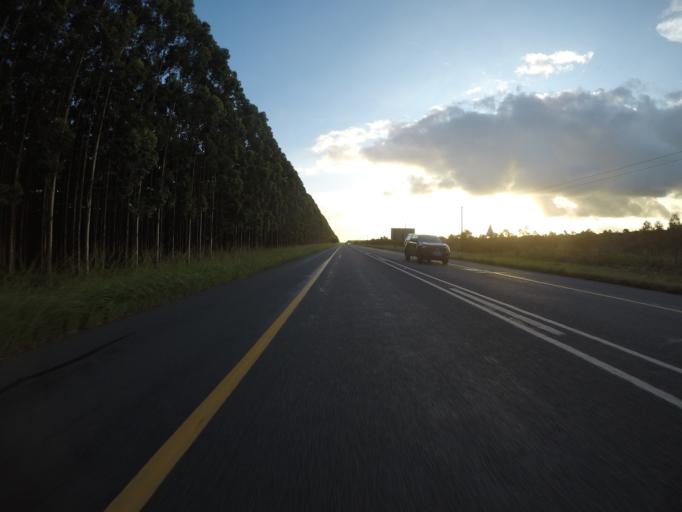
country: ZA
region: KwaZulu-Natal
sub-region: uThungulu District Municipality
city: KwaMbonambi
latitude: -28.6118
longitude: 32.0870
